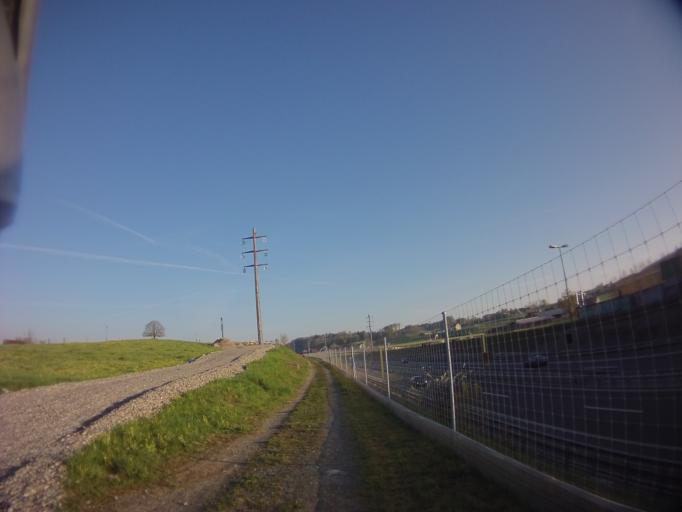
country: CH
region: Zurich
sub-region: Bezirk Affoltern
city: Mettmenstetten
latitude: 47.2445
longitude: 8.4532
